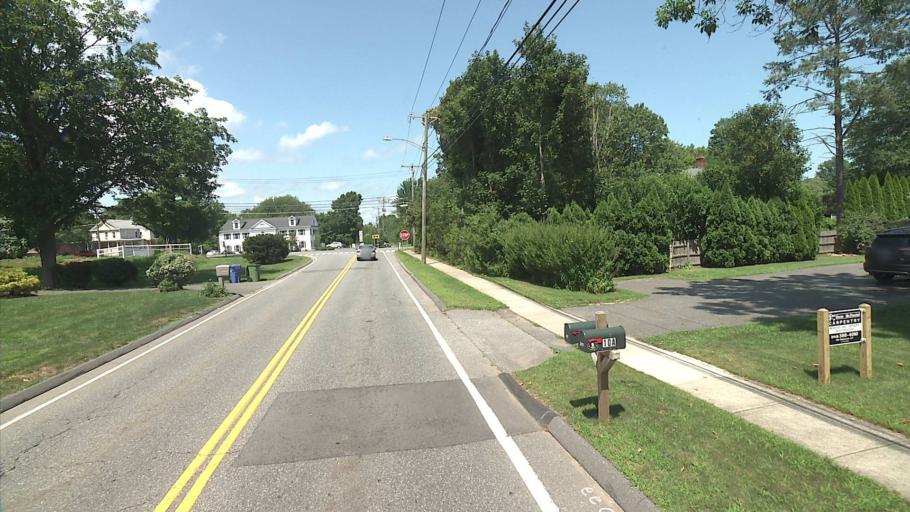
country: US
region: Connecticut
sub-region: Middlesex County
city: Saybrook Manor
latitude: 41.2865
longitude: -72.3899
